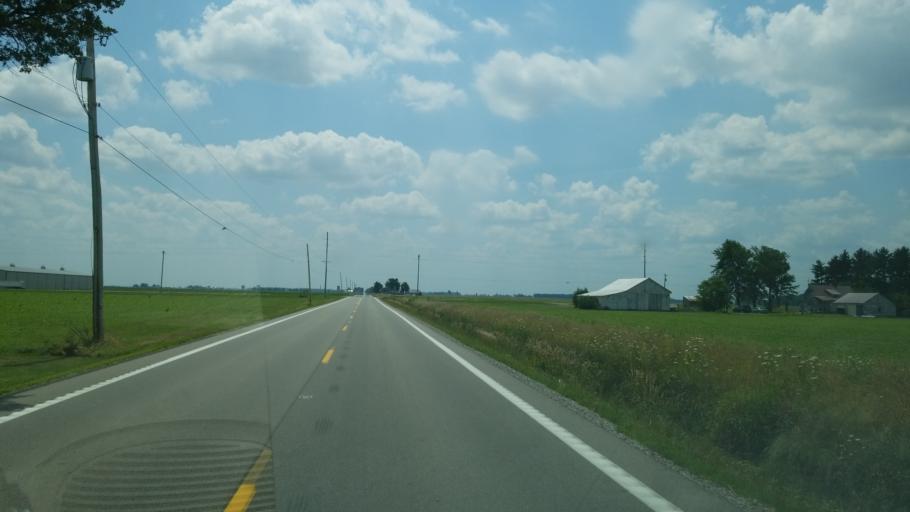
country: US
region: Ohio
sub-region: Henry County
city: Deshler
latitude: 41.3290
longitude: -83.9415
